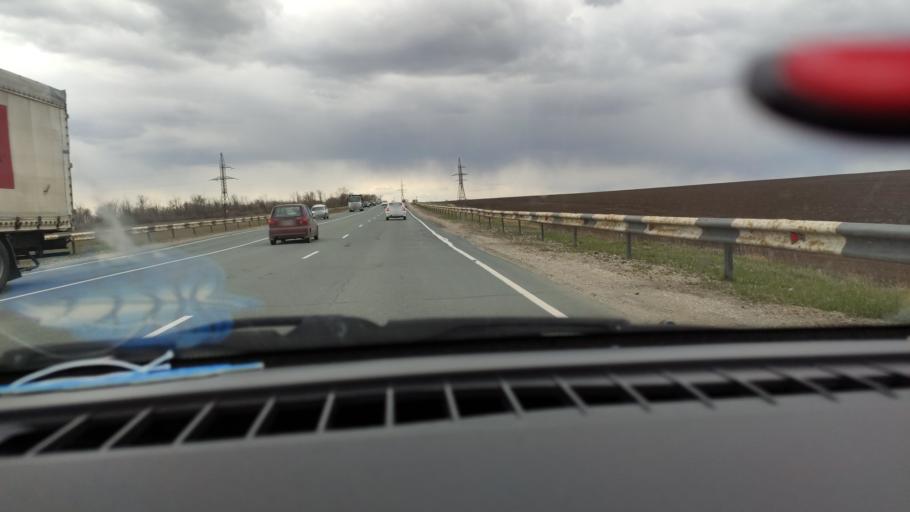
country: RU
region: Saratov
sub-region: Saratovskiy Rayon
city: Saratov
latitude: 51.7473
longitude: 46.0550
